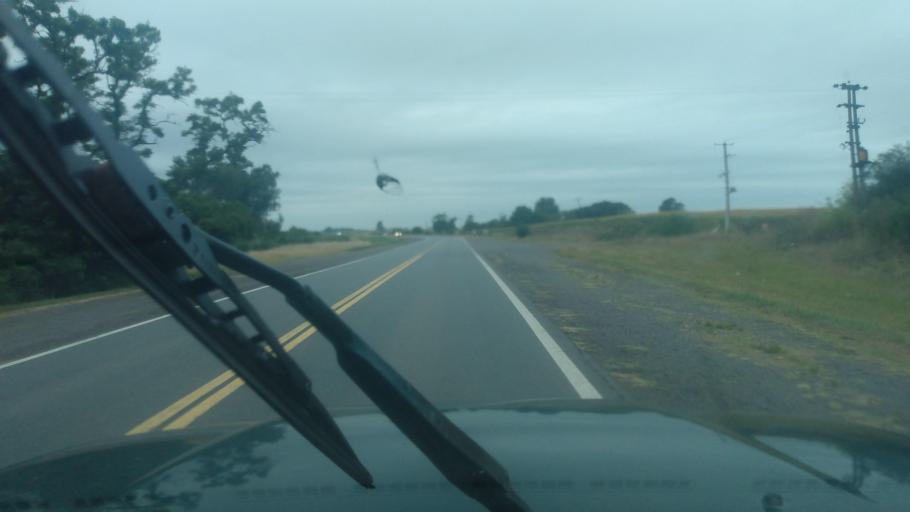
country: AR
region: Buenos Aires
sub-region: Partido de Bragado
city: Bragado
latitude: -35.3234
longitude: -60.6413
